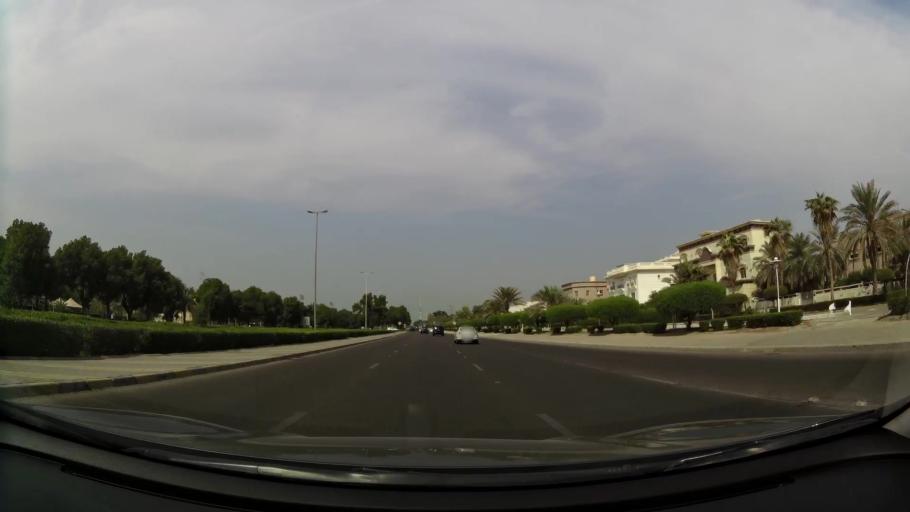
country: KW
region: Muhafazat Hawalli
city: Hawalli
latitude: 29.3233
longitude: 47.9924
